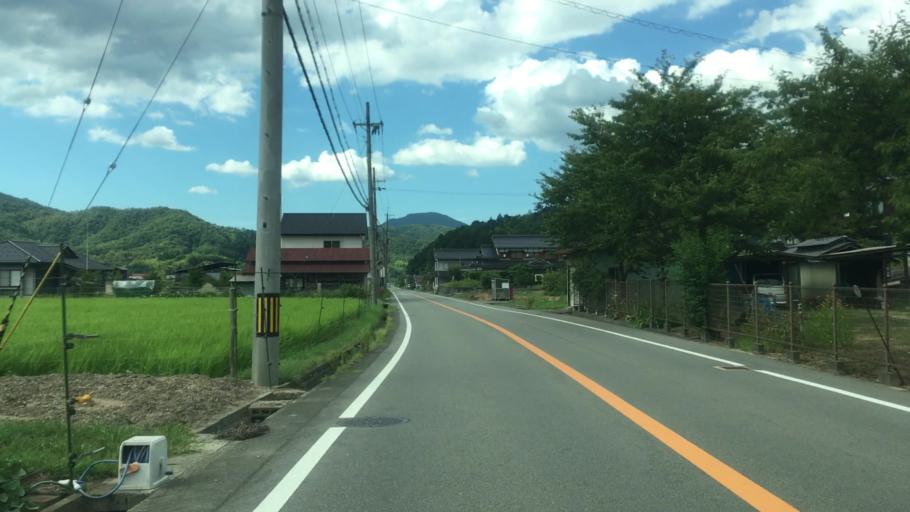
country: JP
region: Hyogo
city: Toyooka
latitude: 35.5410
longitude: 134.7902
